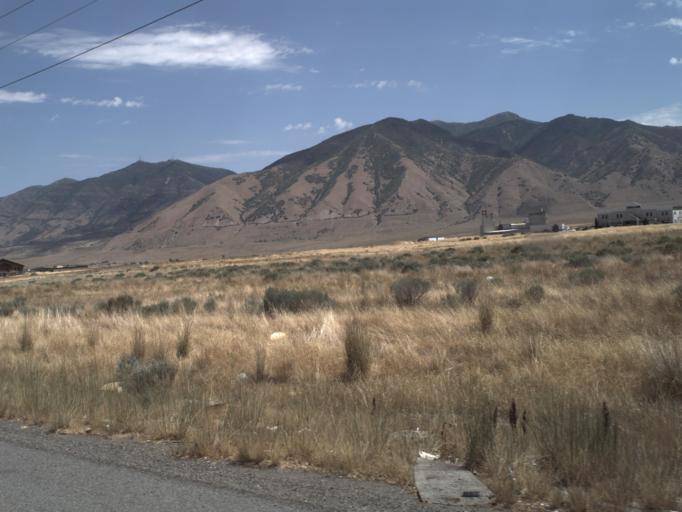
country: US
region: Utah
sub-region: Tooele County
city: Tooele
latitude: 40.5642
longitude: -112.2960
